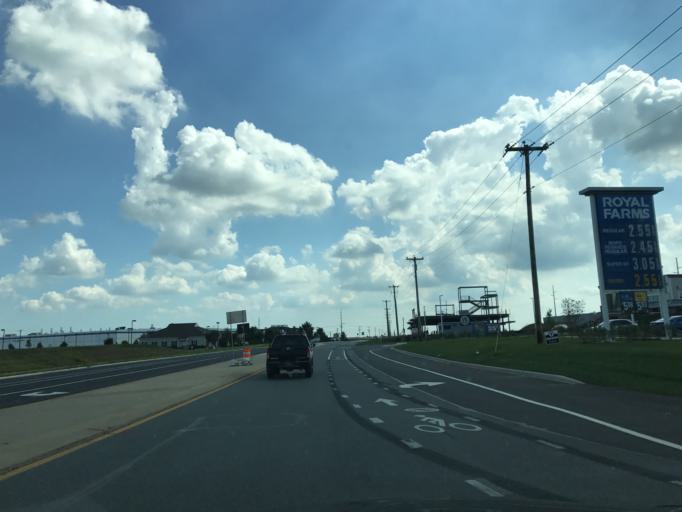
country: US
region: Delaware
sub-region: New Castle County
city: Middletown
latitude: 39.4404
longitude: -75.7469
